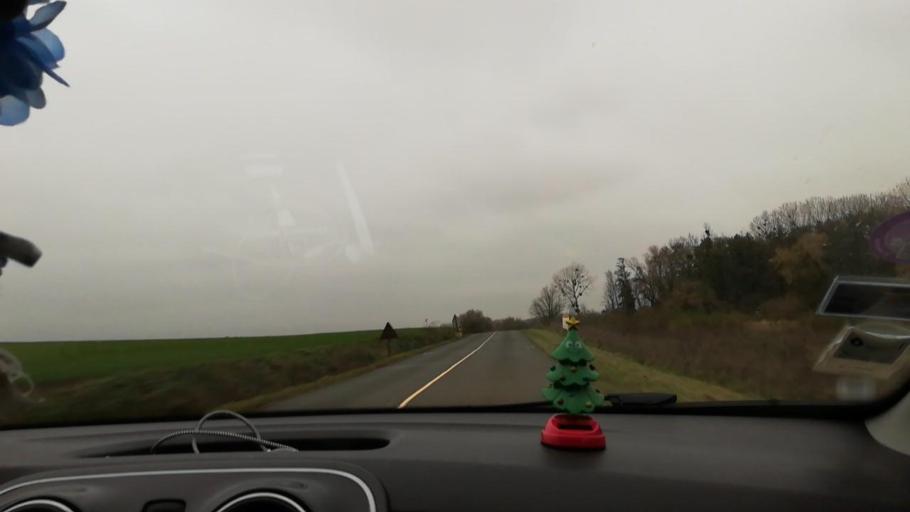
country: FR
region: Ile-de-France
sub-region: Departement de Seine-et-Marne
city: Juilly
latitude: 48.9910
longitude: 2.6941
